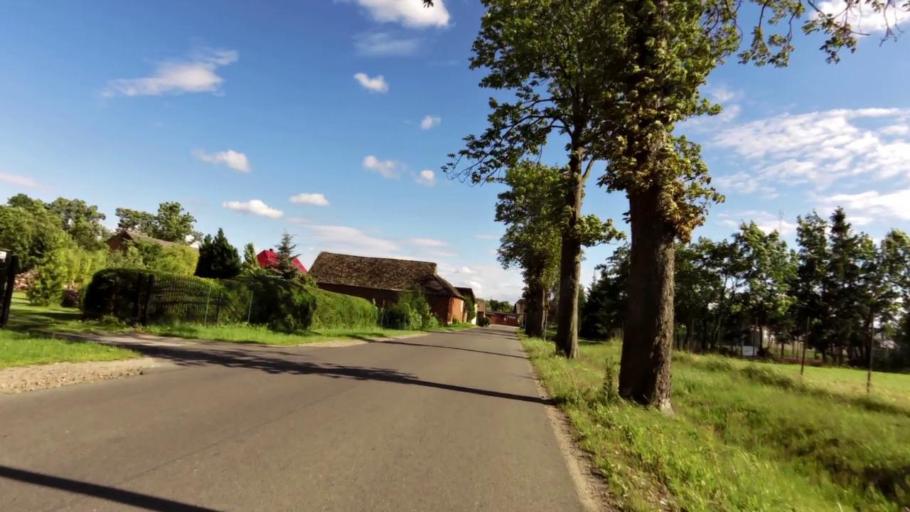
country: PL
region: West Pomeranian Voivodeship
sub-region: Powiat slawienski
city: Slawno
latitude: 54.4359
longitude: 16.7329
